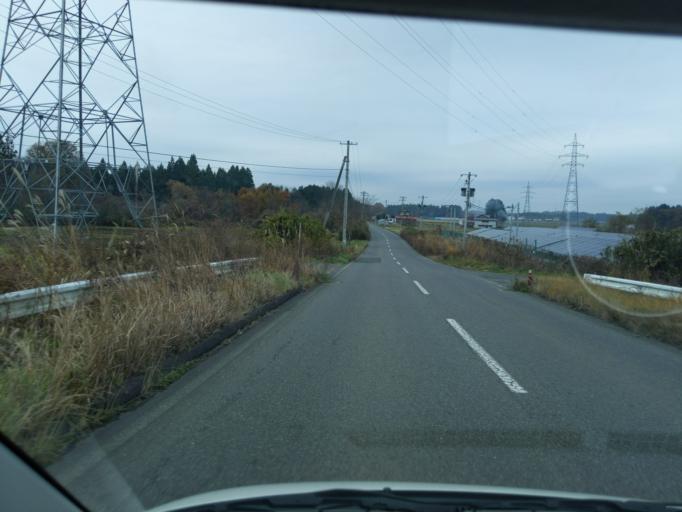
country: JP
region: Iwate
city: Mizusawa
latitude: 39.0960
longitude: 141.1129
